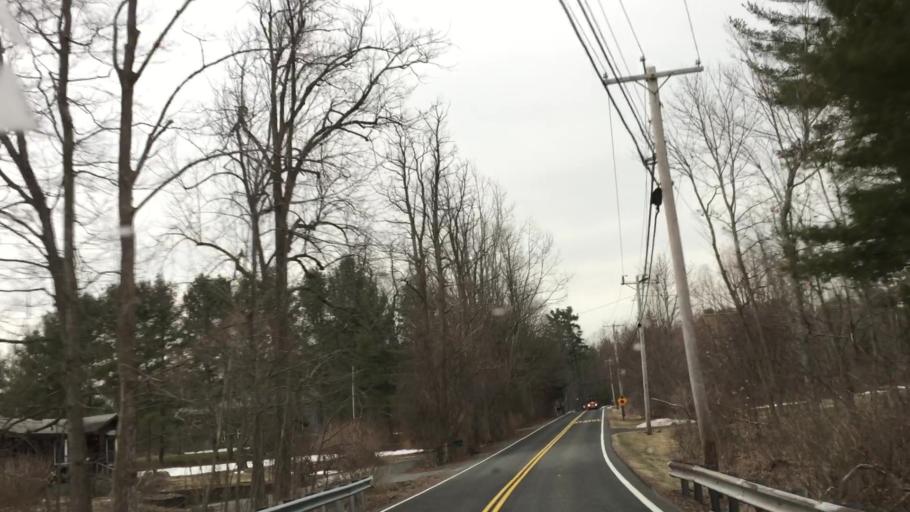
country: US
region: Massachusetts
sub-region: Berkshire County
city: Lenox
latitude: 42.3415
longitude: -73.2549
